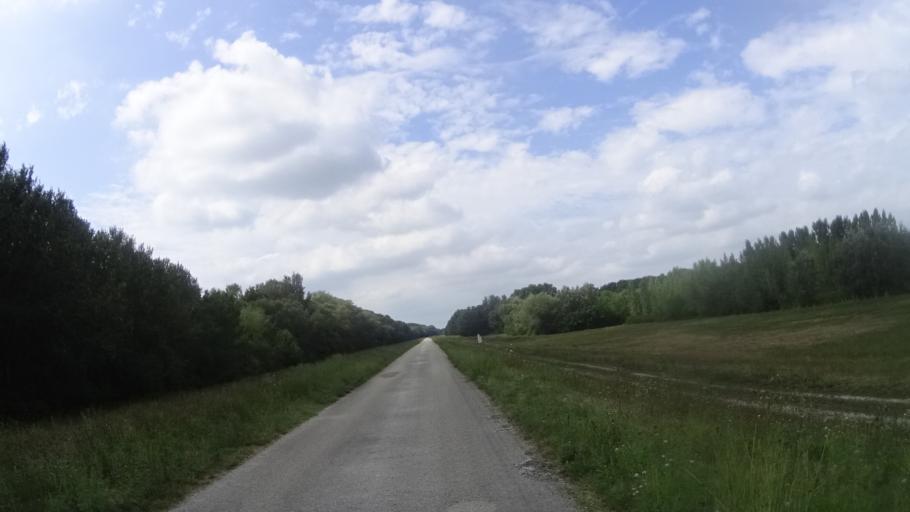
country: SK
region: Trnavsky
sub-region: Okres Dunajska Streda
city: Velky Meder
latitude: 47.7711
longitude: 17.7156
